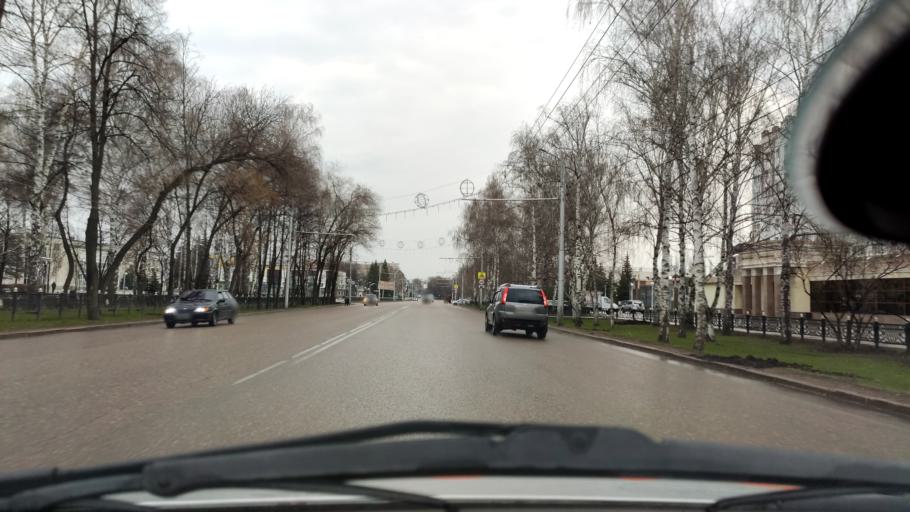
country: RU
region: Bashkortostan
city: Sterlitamak
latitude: 53.6352
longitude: 55.9351
